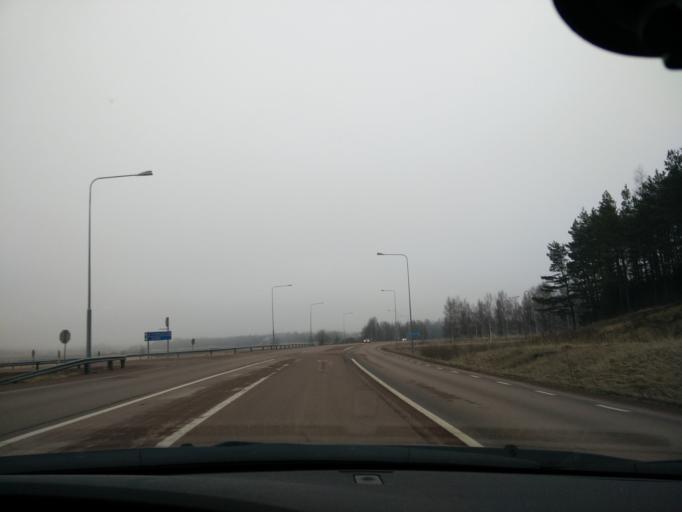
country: AX
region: Alands landsbygd
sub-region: Jomala
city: Jomala
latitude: 60.1432
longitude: 19.9347
